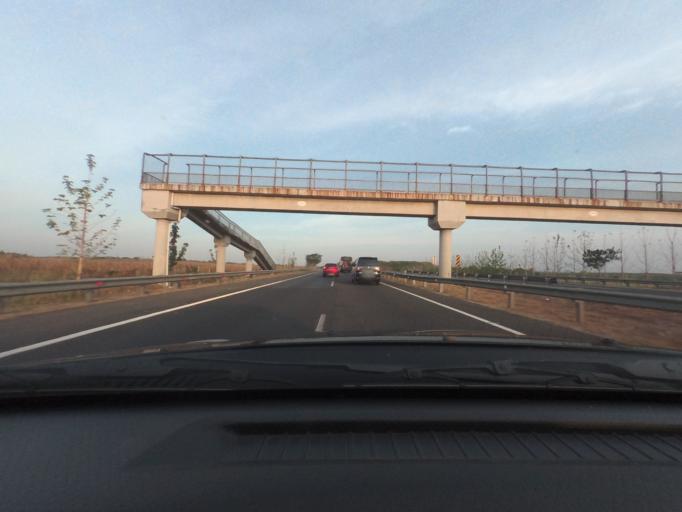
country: ID
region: West Java
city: Pamanukan
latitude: -6.5359
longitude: 107.8359
